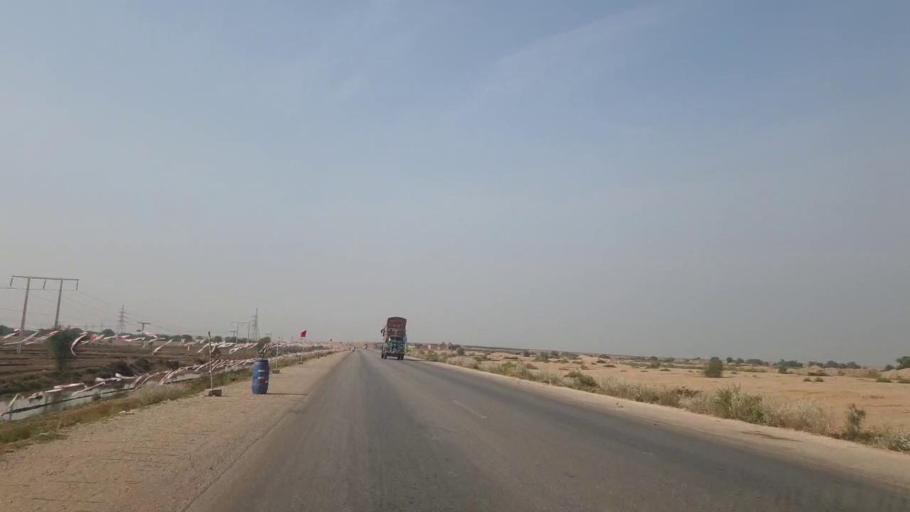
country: PK
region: Sindh
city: Sann
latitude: 26.1499
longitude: 68.0291
